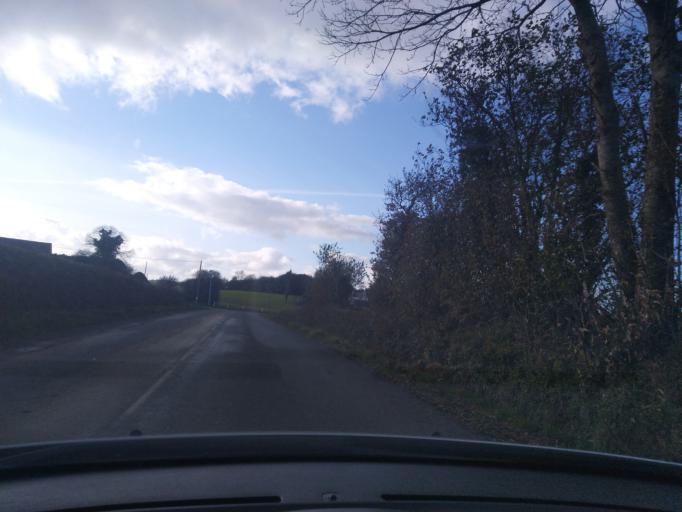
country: FR
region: Brittany
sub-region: Departement du Finistere
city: Plouigneau
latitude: 48.5729
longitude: -3.6497
